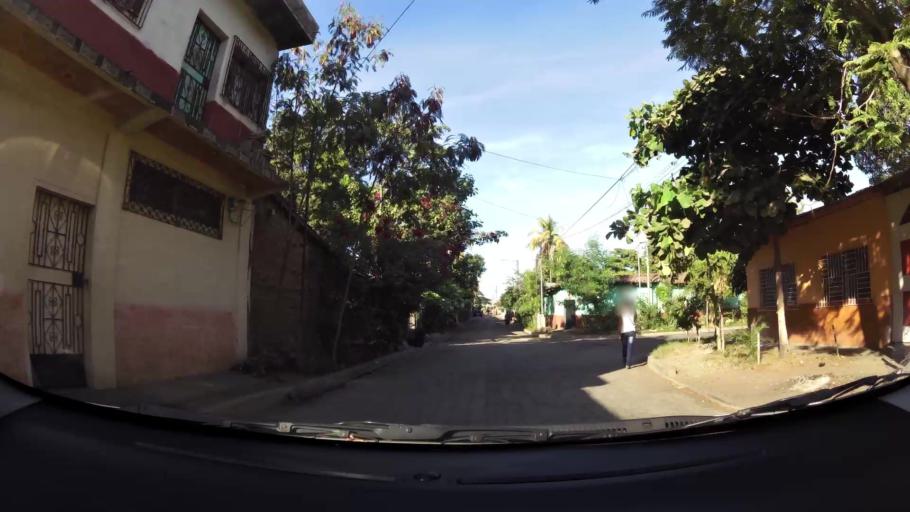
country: SV
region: San Miguel
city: San Miguel
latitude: 13.4631
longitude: -88.1762
